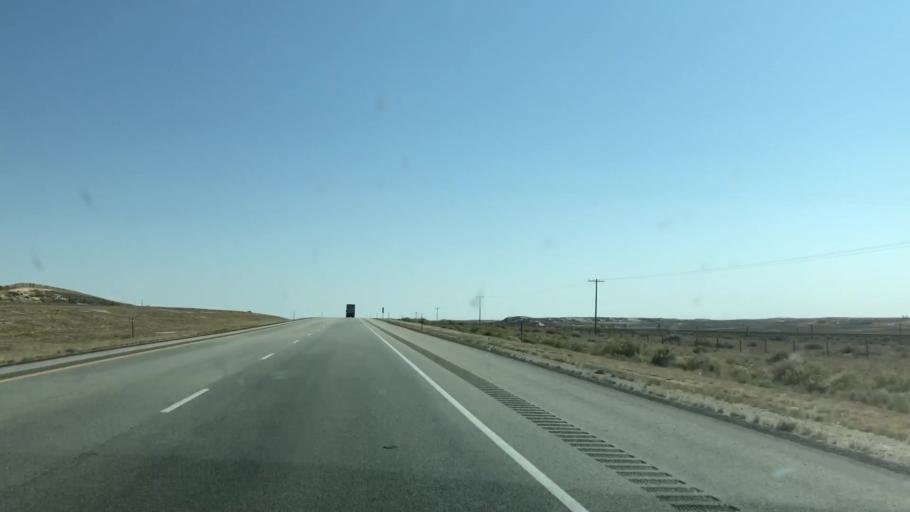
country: US
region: Wyoming
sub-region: Carbon County
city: Rawlins
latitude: 41.6970
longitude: -107.9210
